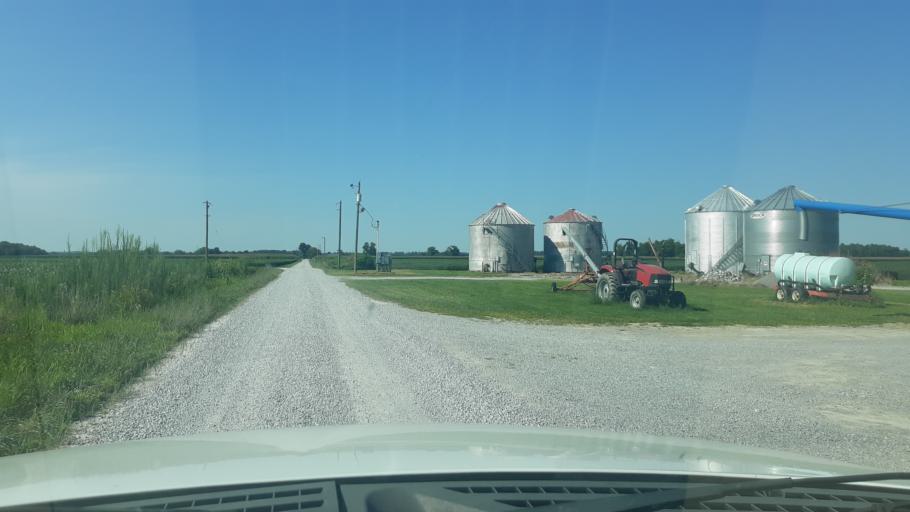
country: US
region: Illinois
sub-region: Saline County
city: Eldorado
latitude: 37.8512
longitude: -88.4849
